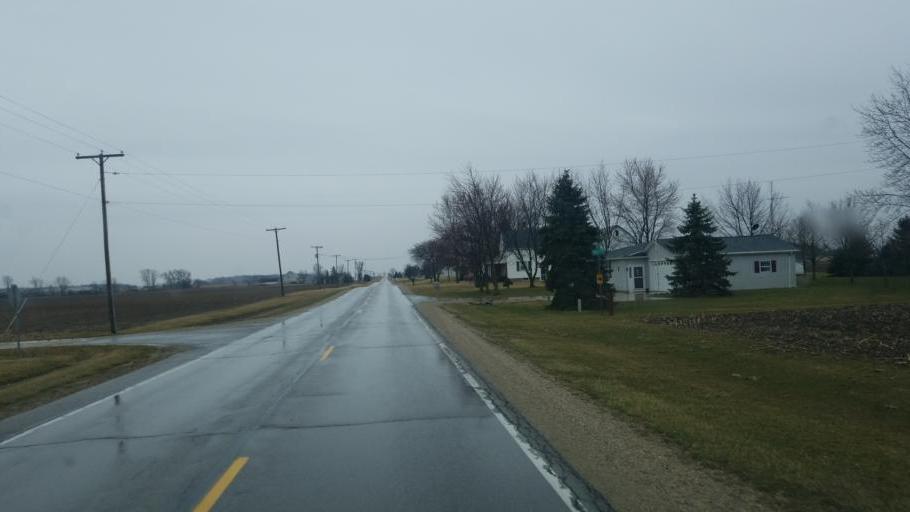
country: US
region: Indiana
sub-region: Adams County
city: Geneva
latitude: 40.6199
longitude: -85.0412
